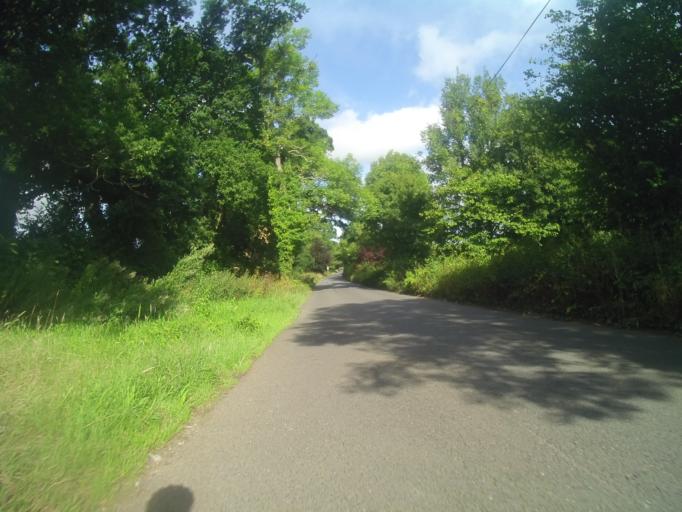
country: GB
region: England
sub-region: Devon
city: Totnes
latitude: 50.4362
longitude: -3.6997
